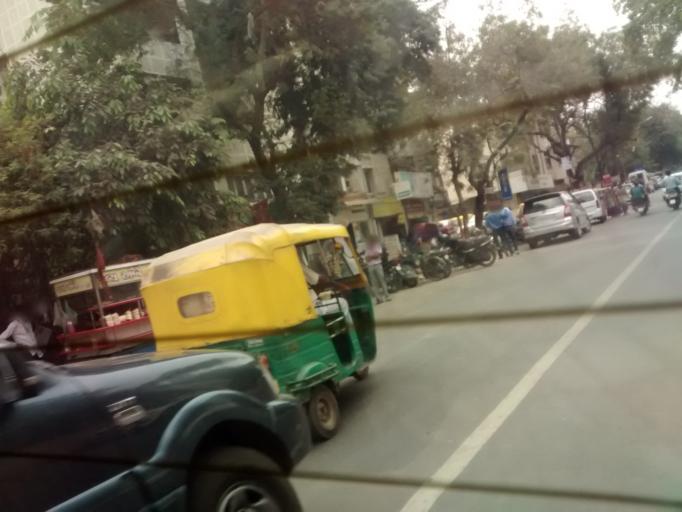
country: IN
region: Gujarat
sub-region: Ahmadabad
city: Ahmedabad
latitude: 23.0401
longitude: 72.5587
